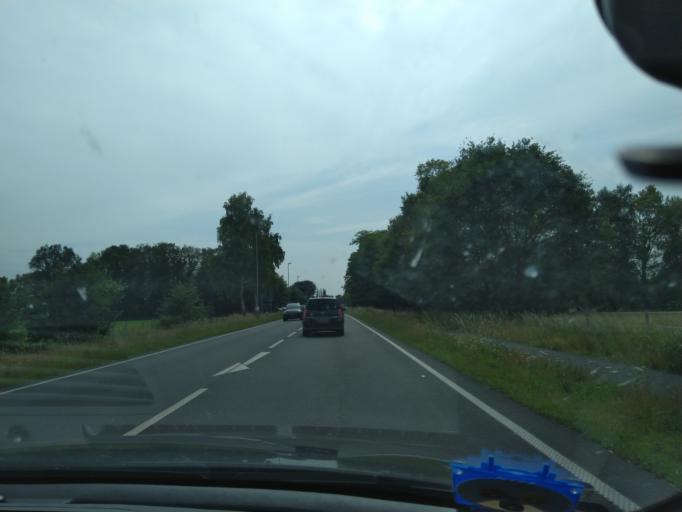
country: DE
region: Lower Saxony
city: Nordhorn
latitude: 52.4061
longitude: 7.0382
